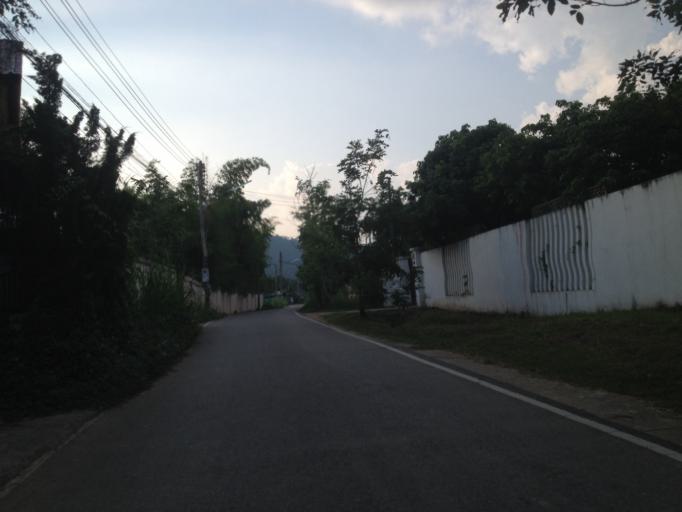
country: TH
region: Chiang Mai
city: Hang Dong
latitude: 18.7477
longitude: 98.9321
